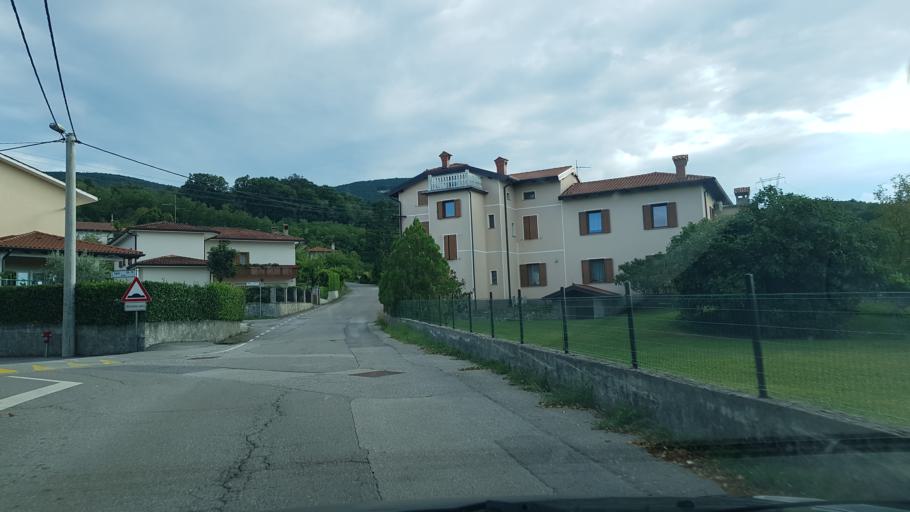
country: SI
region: Rence-Vogrsko
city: Rence
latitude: 45.8812
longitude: 13.6664
